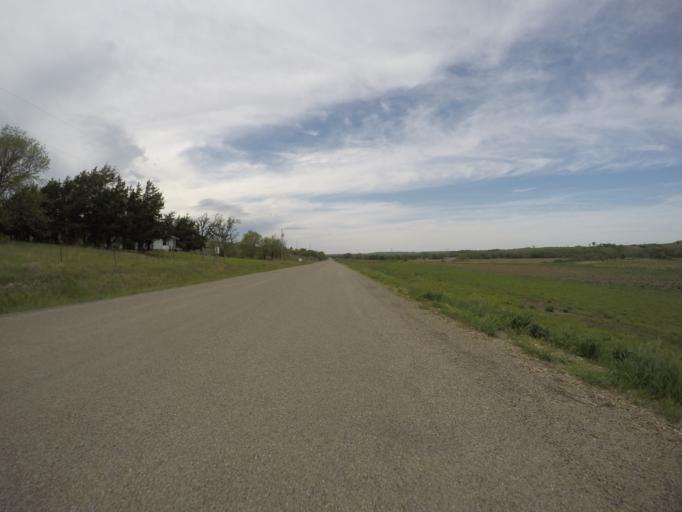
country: US
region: Kansas
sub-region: Riley County
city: Ogden
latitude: 39.0162
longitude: -96.6060
